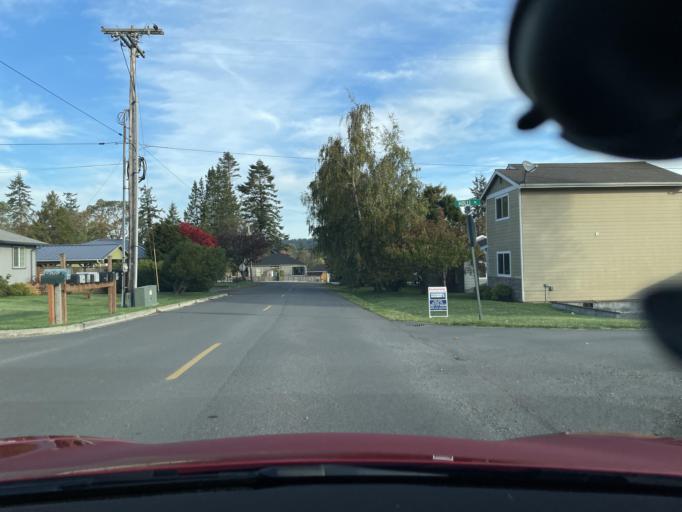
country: US
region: Washington
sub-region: San Juan County
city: Friday Harbor
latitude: 48.5338
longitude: -123.0243
